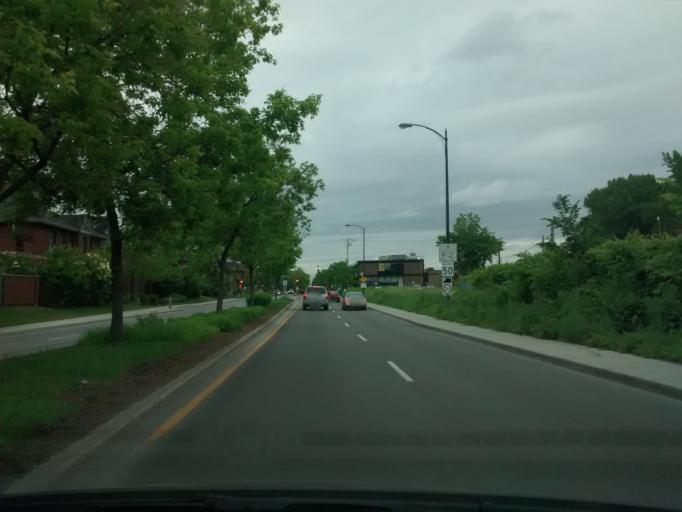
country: CA
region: Quebec
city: Mont-Royal
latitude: 45.5146
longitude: -73.6315
